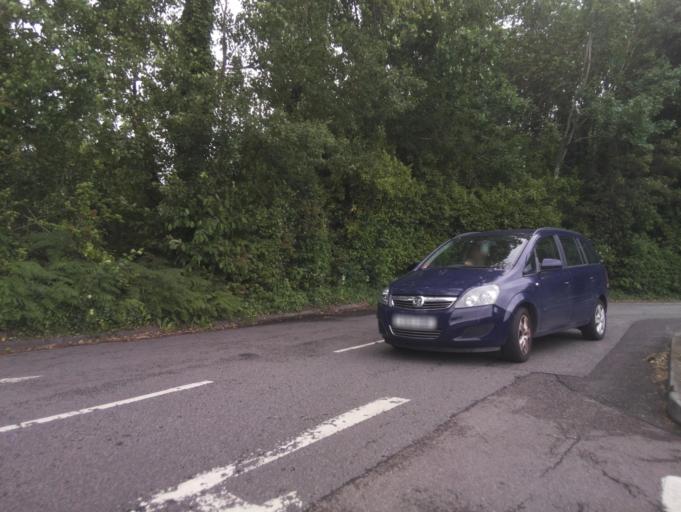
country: GB
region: Wales
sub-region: Vale of Glamorgan
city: Penarth
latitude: 51.4465
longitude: -3.1875
